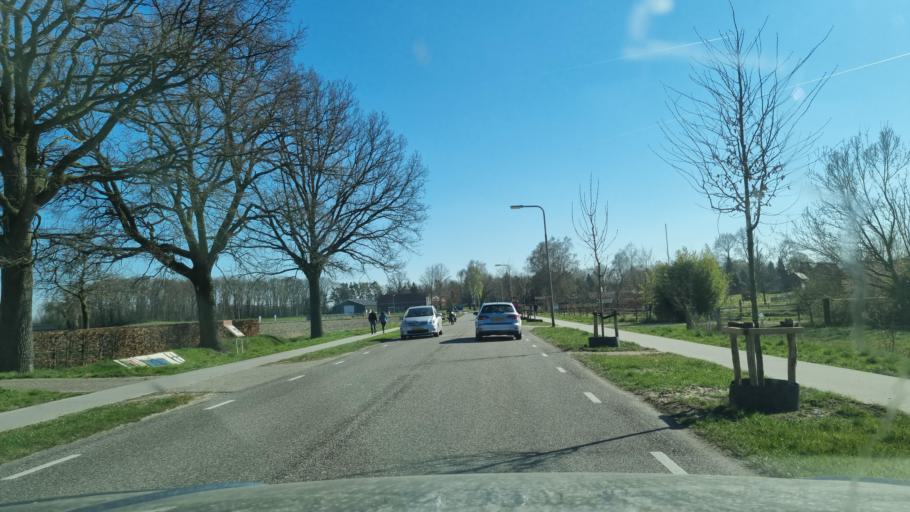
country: NL
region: Gelderland
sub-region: Gemeente Groesbeek
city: Bredeweg
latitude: 51.7321
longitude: 5.9557
